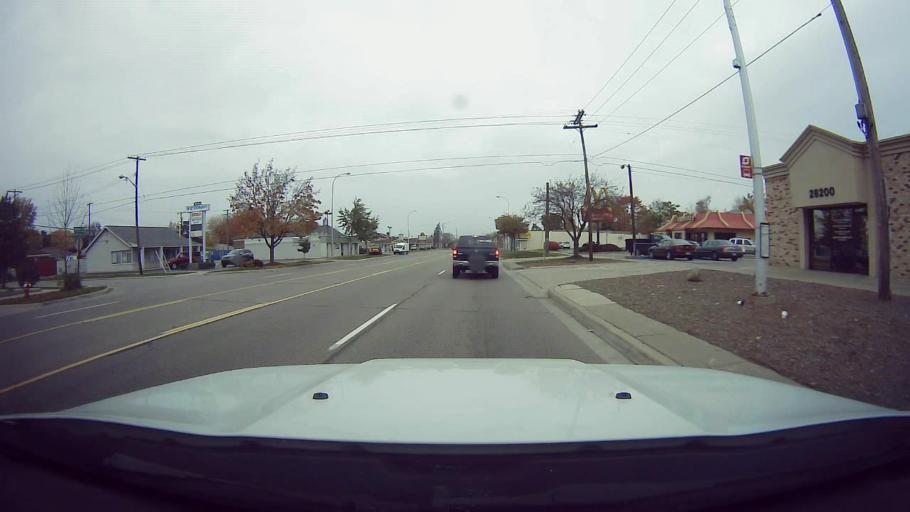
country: US
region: Michigan
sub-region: Oakland County
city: Madison Heights
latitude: 42.5006
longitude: -83.1055
